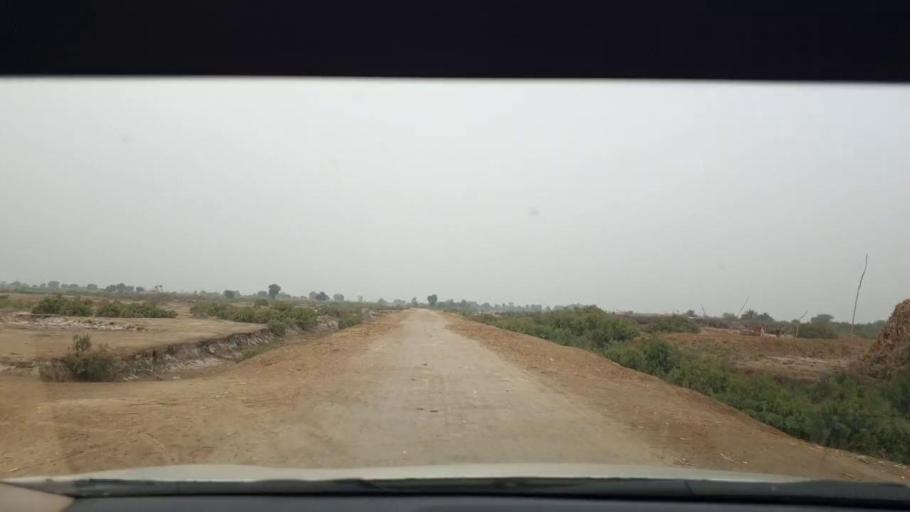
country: PK
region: Sindh
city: Berani
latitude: 25.8488
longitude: 68.8653
